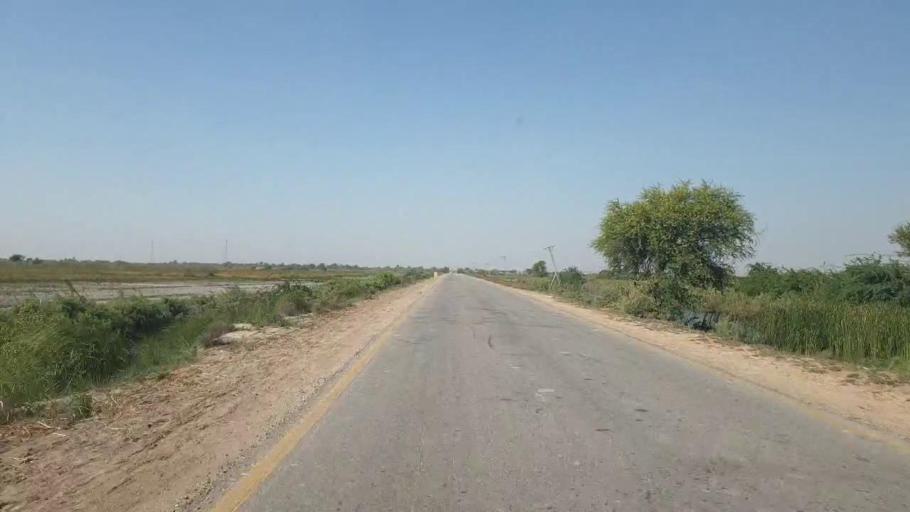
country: PK
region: Sindh
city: Rajo Khanani
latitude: 25.0524
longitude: 68.8066
